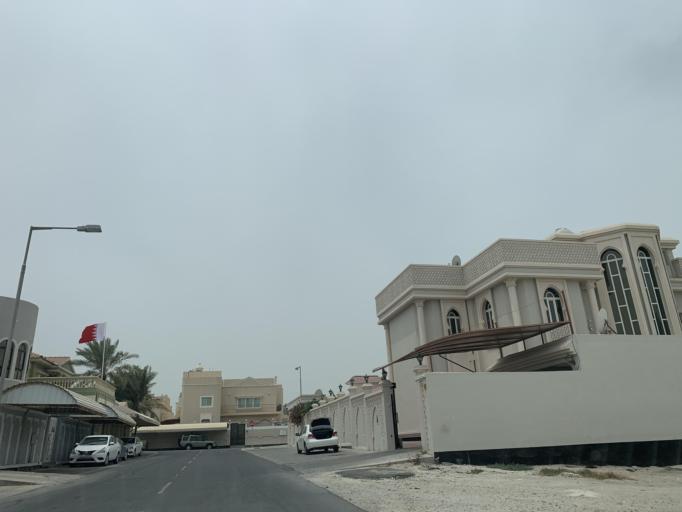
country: BH
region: Northern
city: Ar Rifa'
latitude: 26.1387
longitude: 50.5524
